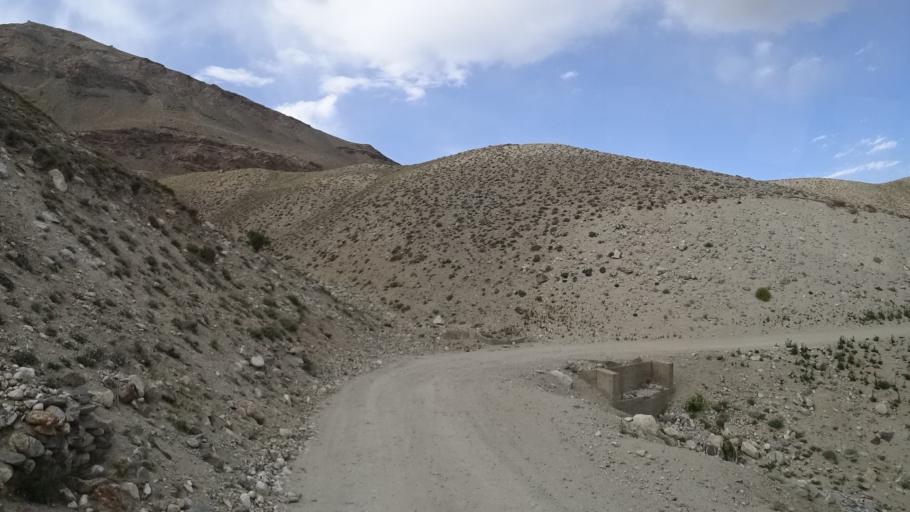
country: AF
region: Badakhshan
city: Khandud
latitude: 37.2224
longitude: 72.7913
